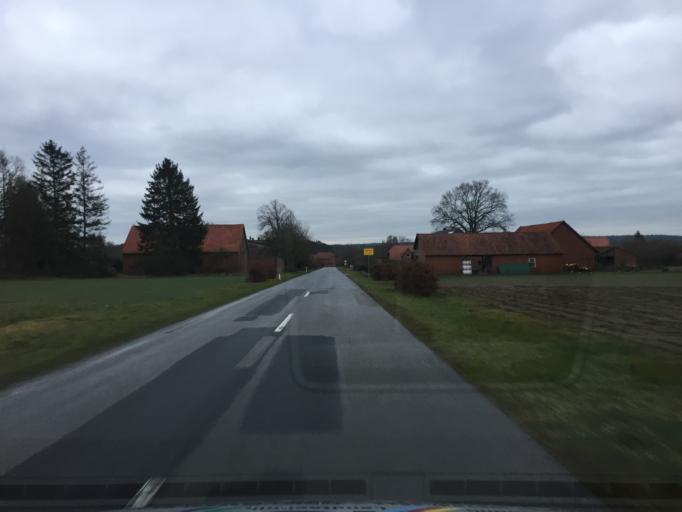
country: DE
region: Lower Saxony
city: Pennigsehl
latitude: 52.6363
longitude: 9.0064
